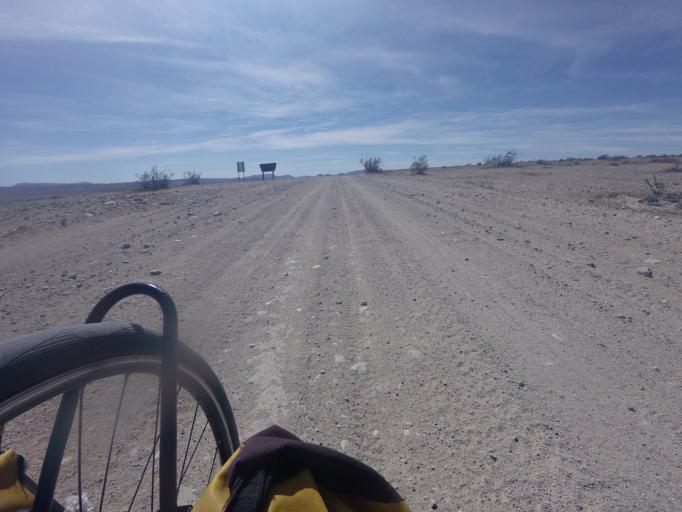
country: US
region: California
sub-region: San Bernardino County
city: Searles Valley
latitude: 35.6013
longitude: -117.3822
